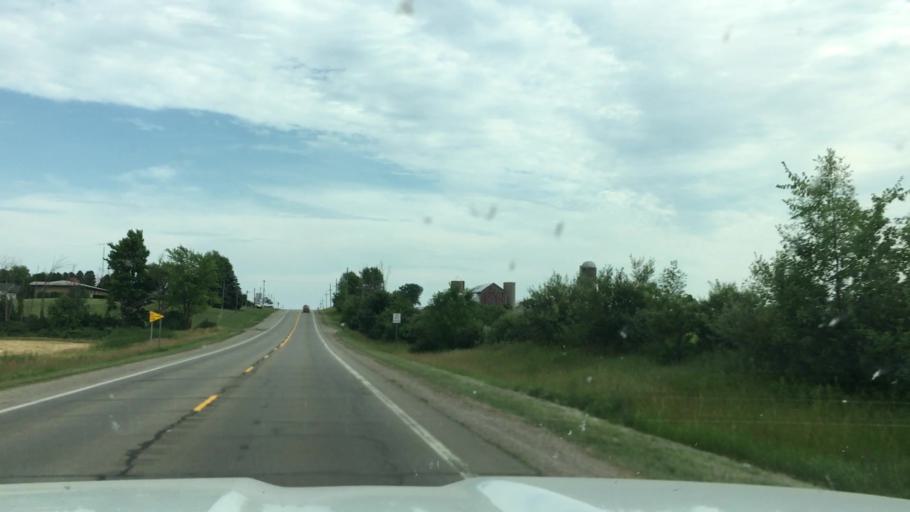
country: US
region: Michigan
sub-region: Sanilac County
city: Marlette
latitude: 43.3110
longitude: -83.0798
